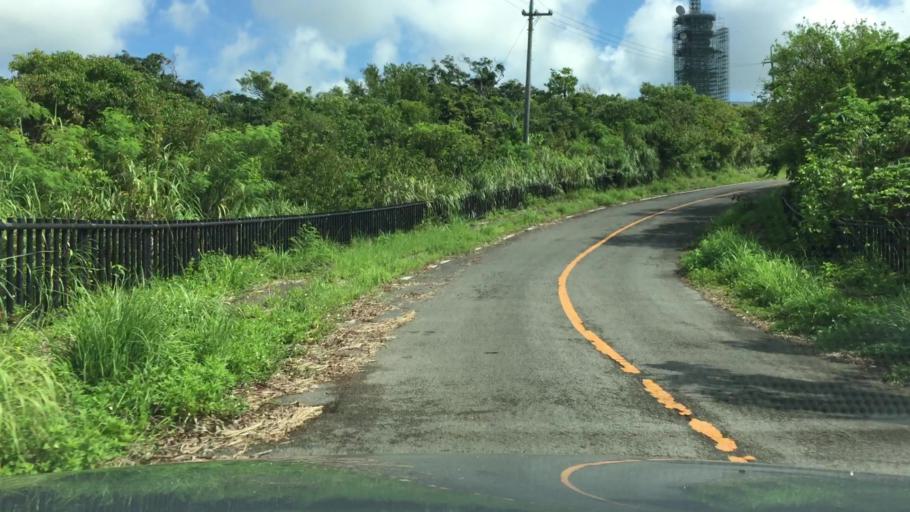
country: JP
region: Okinawa
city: Ishigaki
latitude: 24.3758
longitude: 124.1639
